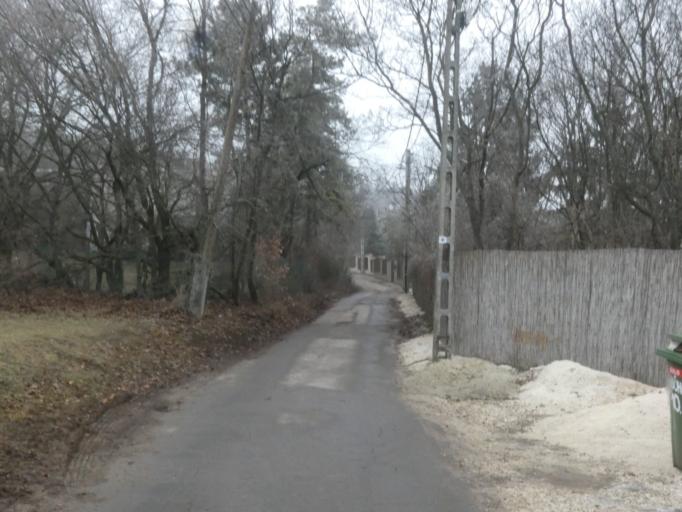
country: HU
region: Budapest
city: Budapest III. keruelet
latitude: 47.5392
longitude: 19.0164
